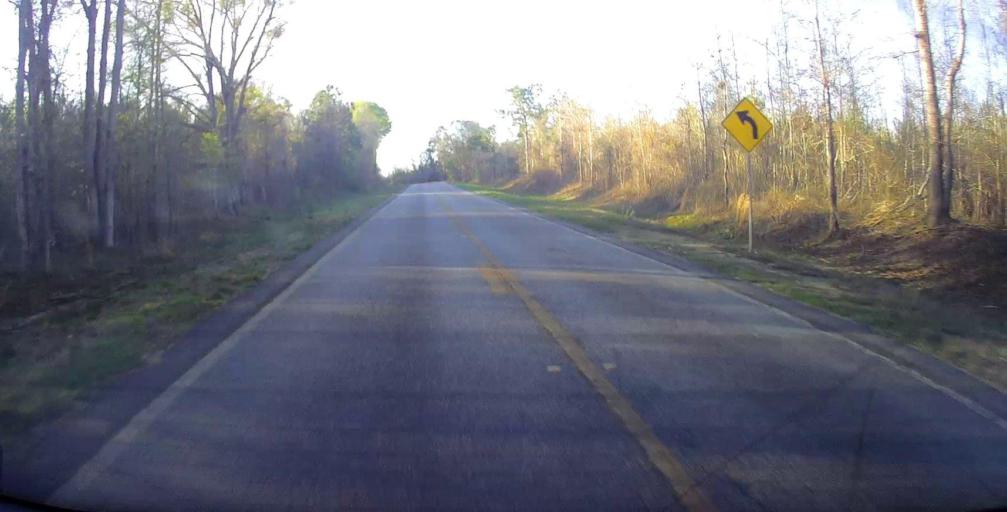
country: US
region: Georgia
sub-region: Wilcox County
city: Abbeville
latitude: 32.1011
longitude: -83.3046
